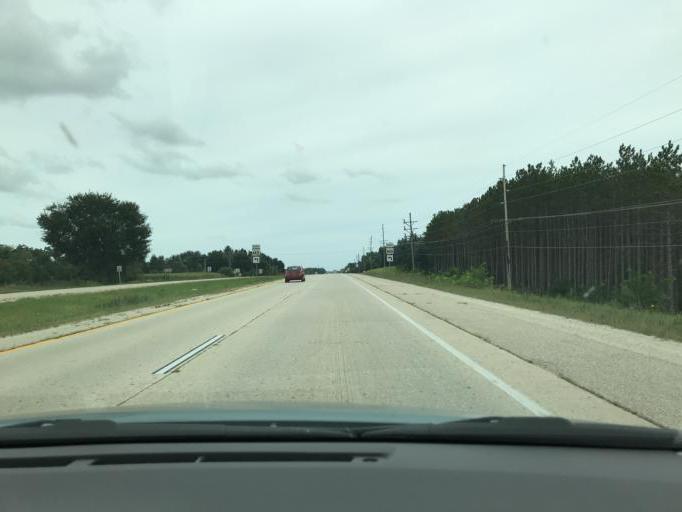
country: US
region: Wisconsin
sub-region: Kenosha County
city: Bristol
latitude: 42.5674
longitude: -88.0001
